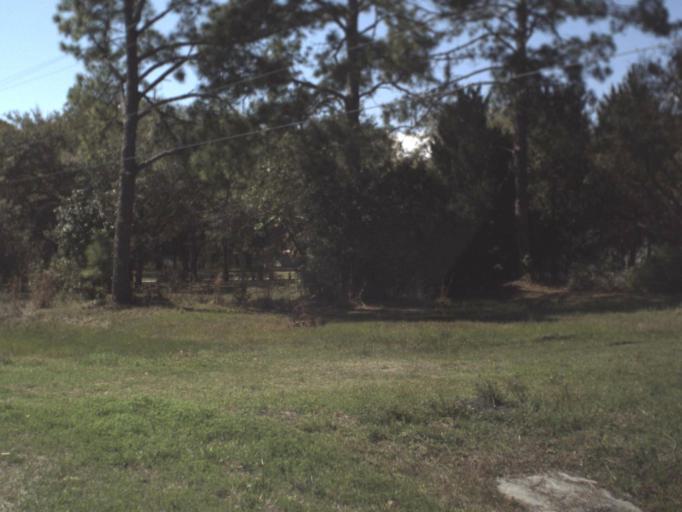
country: US
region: Florida
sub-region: Franklin County
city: Carrabelle
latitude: 29.8880
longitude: -84.5803
